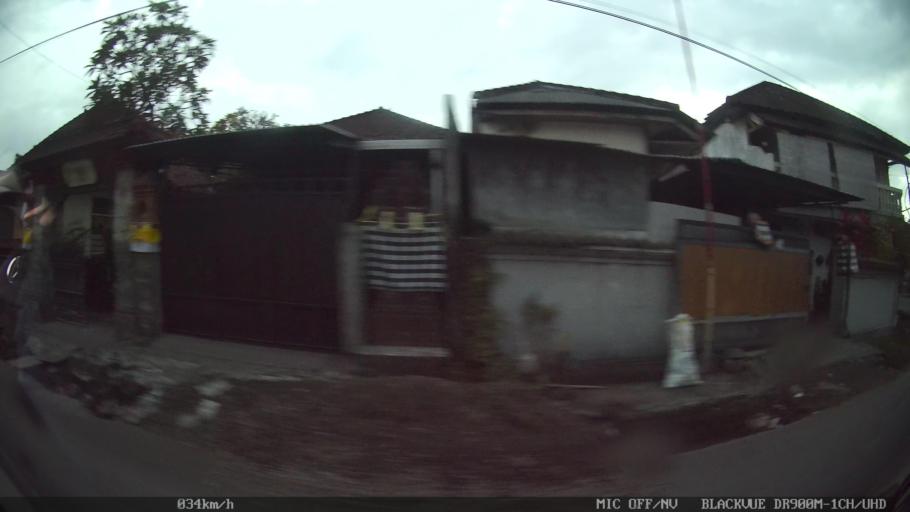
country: ID
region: Bali
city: Banjar Kertajiwa
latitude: -8.6402
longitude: 115.2671
